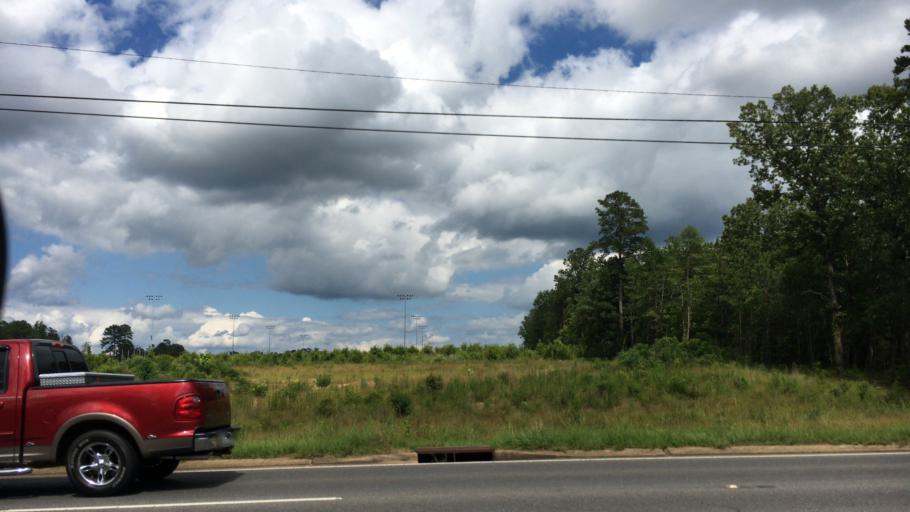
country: US
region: Louisiana
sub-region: Lincoln Parish
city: Ruston
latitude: 32.5024
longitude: -92.6370
